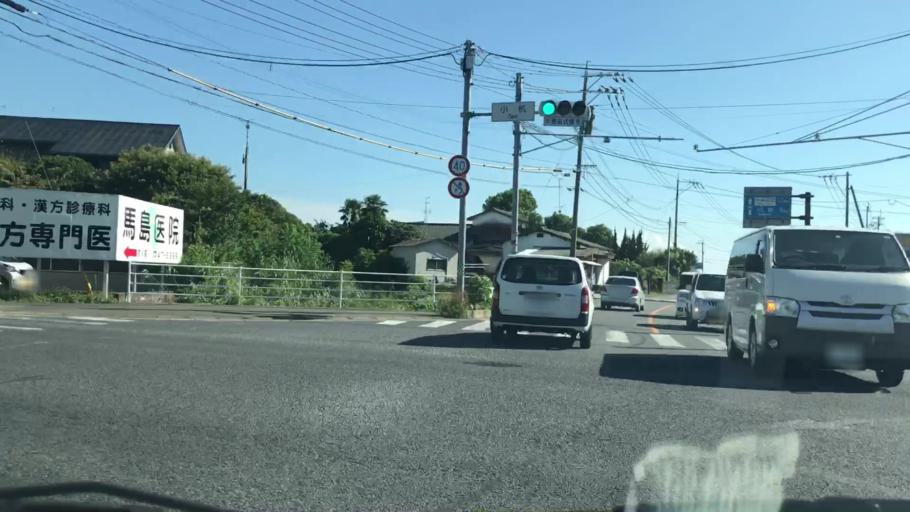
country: JP
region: Saga Prefecture
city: Okawa
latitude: 33.2236
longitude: 130.3517
